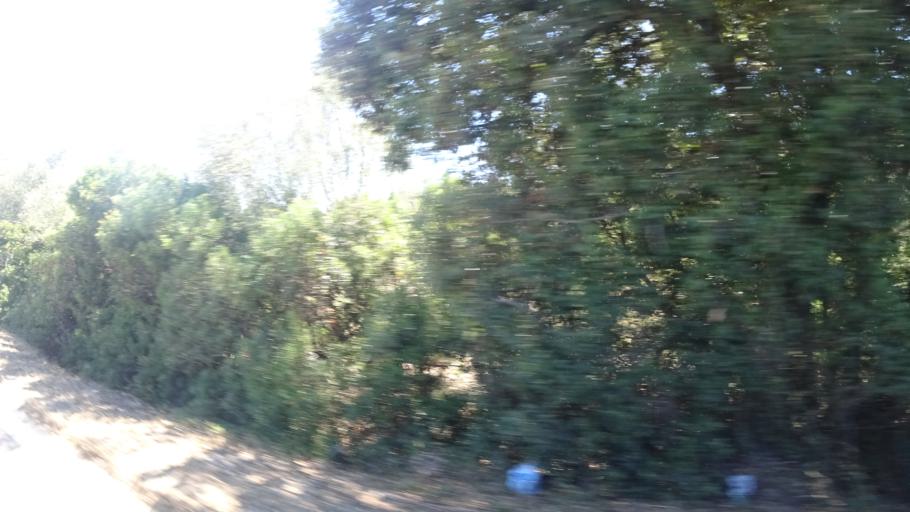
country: FR
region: Corsica
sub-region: Departement de la Corse-du-Sud
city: Alata
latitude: 41.9559
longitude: 8.7287
